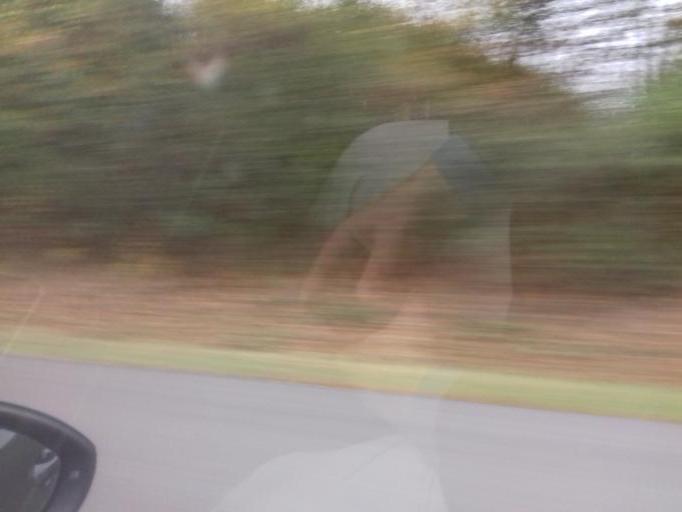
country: LU
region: Grevenmacher
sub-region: Canton de Grevenmacher
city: Flaxweiler
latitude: 49.6485
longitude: 6.3306
